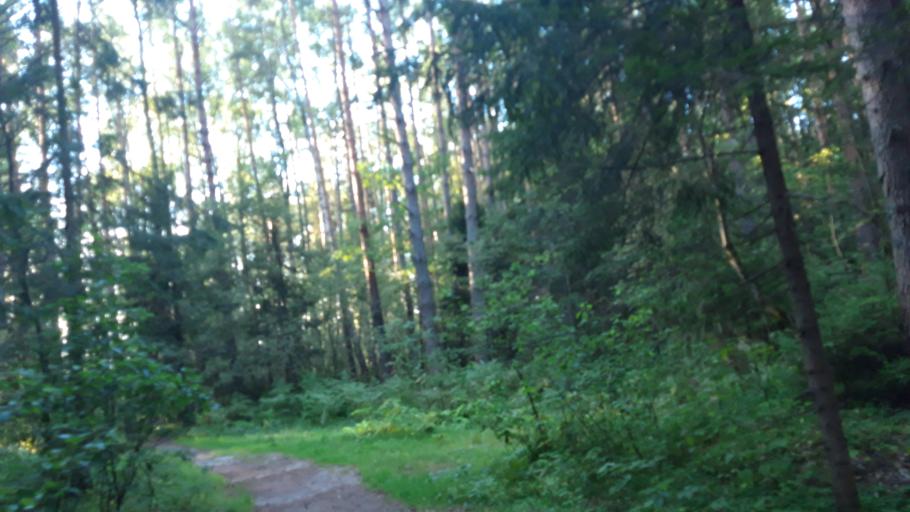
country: RU
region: Tverskaya
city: Konakovo
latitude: 56.6746
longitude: 36.6893
